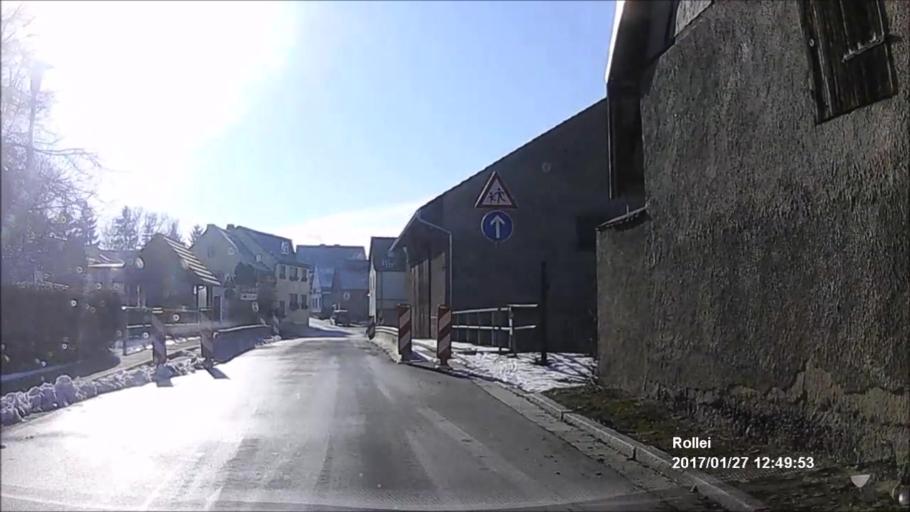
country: DE
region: Thuringia
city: Bruchstedt
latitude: 51.1835
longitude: 10.7869
